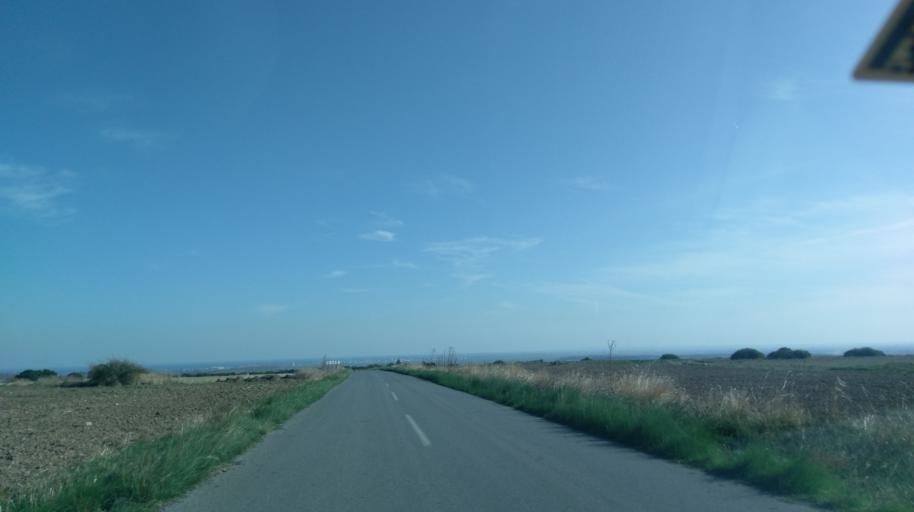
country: CY
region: Ammochostos
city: Trikomo
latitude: 35.3169
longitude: 33.8244
